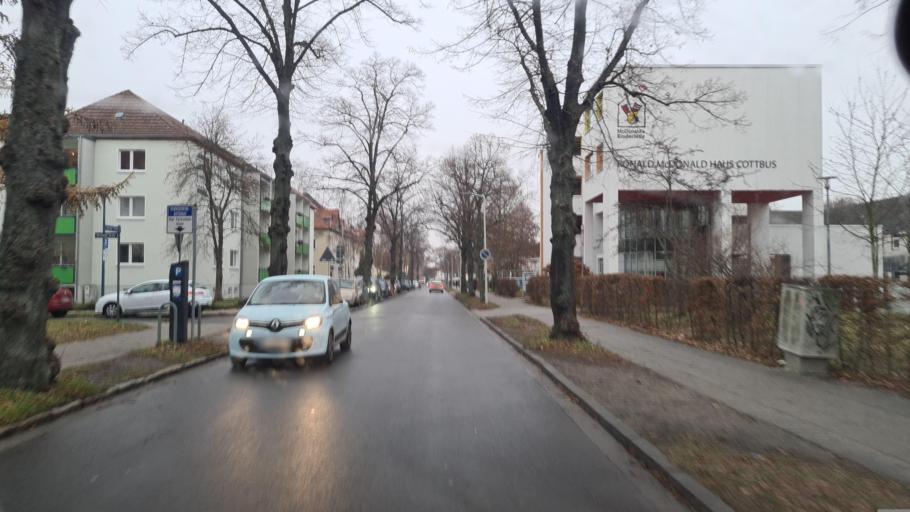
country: DE
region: Brandenburg
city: Cottbus
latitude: 51.7444
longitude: 14.3233
